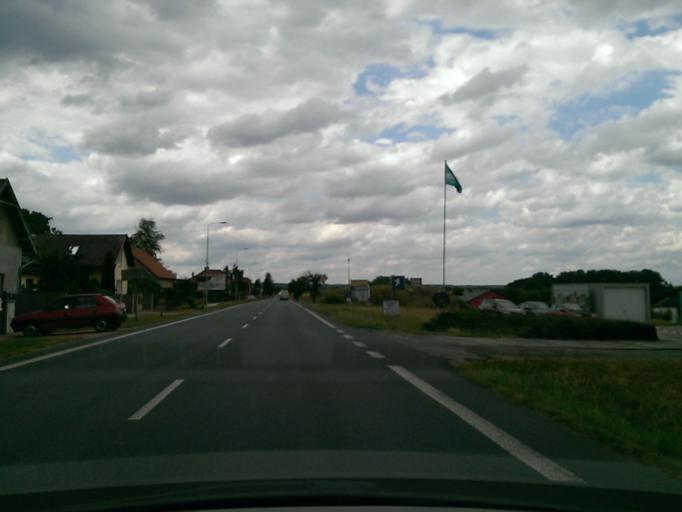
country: CZ
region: Central Bohemia
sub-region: Okres Nymburk
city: Nymburk
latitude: 50.2214
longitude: 15.0284
